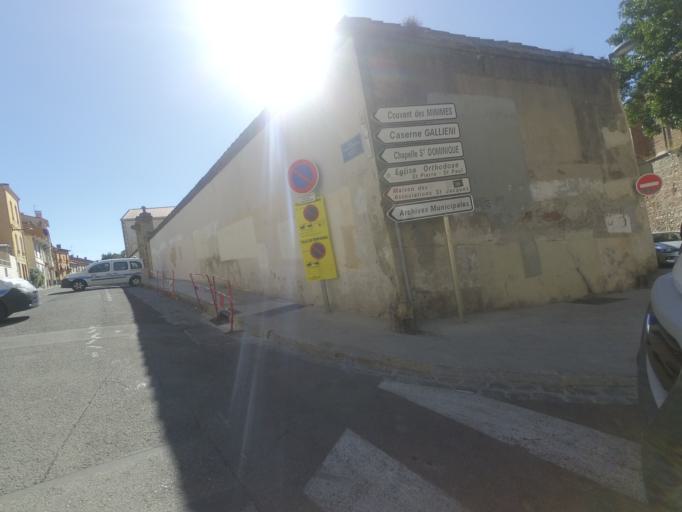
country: FR
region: Languedoc-Roussillon
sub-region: Departement des Pyrenees-Orientales
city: Perpignan
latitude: 42.7008
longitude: 2.8980
